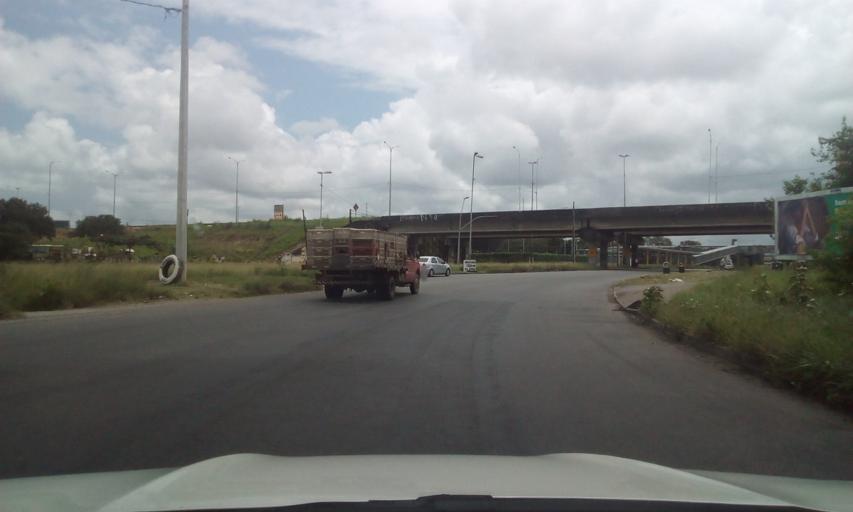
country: BR
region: Pernambuco
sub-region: Abreu E Lima
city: Abreu e Lima
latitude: -7.9218
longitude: -34.8927
